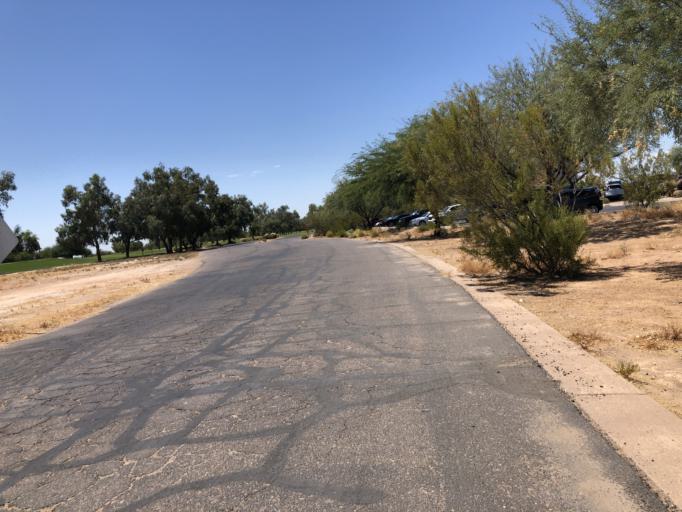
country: US
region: Arizona
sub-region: Maricopa County
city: Scottsdale
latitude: 33.5463
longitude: -111.8643
